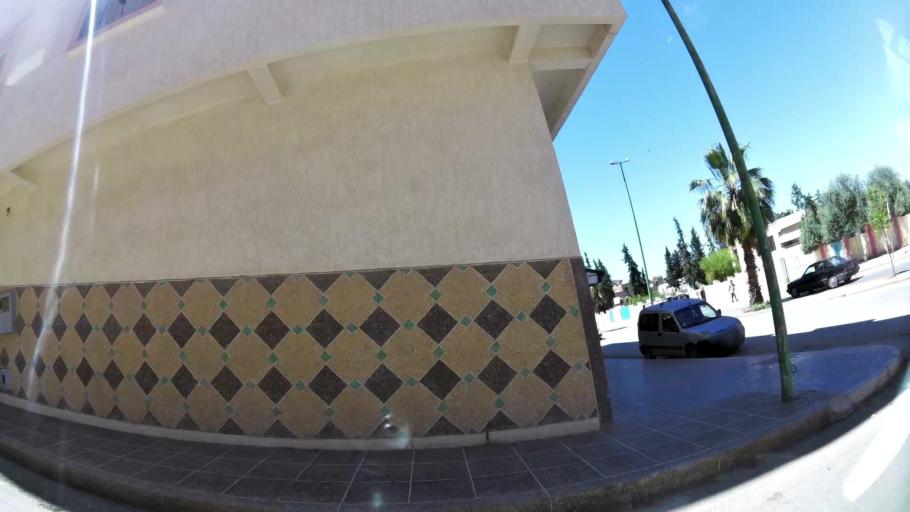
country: MA
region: Meknes-Tafilalet
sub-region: Meknes
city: Meknes
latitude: 33.8977
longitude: -5.5772
